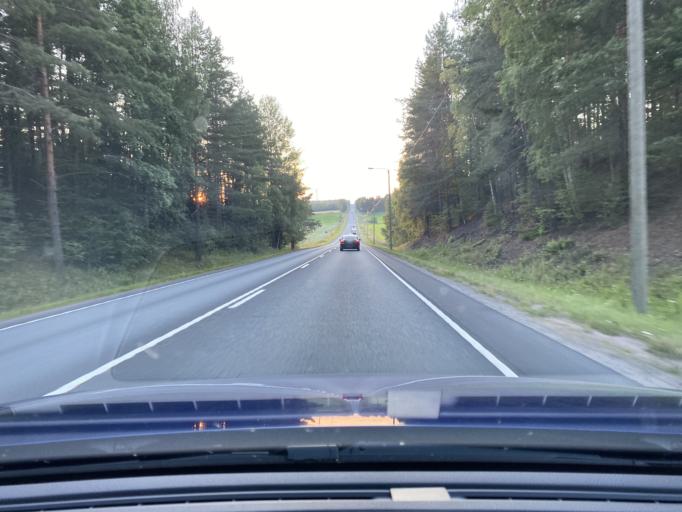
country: FI
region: Pirkanmaa
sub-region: Luoteis-Pirkanmaa
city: Ikaalinen
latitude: 61.7651
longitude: 23.0199
